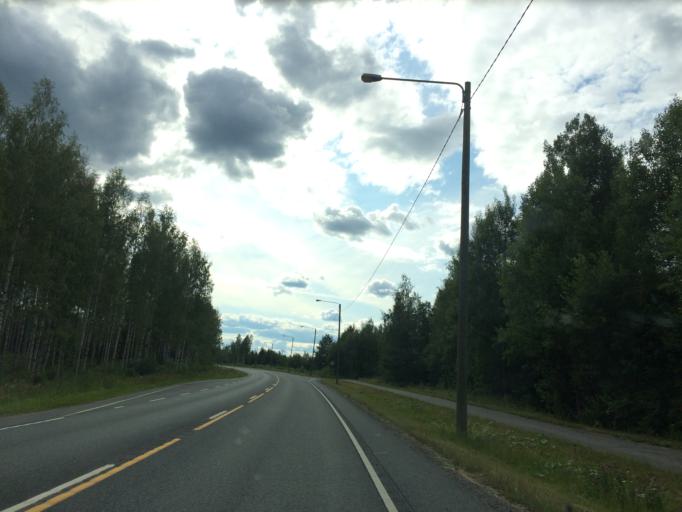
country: FI
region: Haeme
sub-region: Haemeenlinna
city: Janakkala
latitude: 60.9228
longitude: 24.5937
